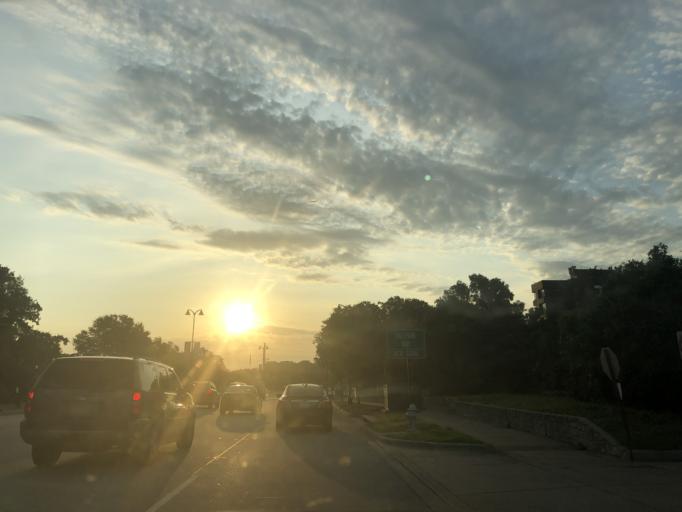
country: US
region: Texas
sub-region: Tarrant County
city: Arlington
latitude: 32.7627
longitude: -97.0785
